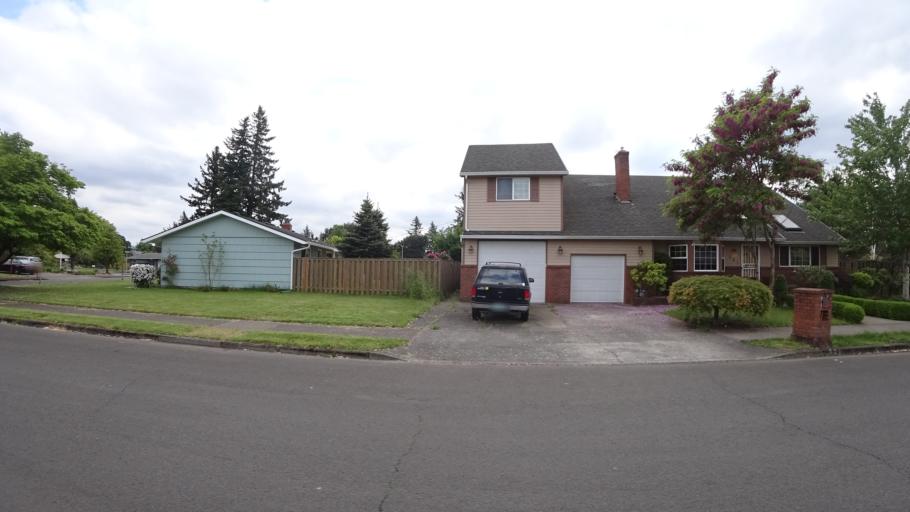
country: US
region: Oregon
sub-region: Multnomah County
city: Fairview
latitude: 45.5160
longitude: -122.4901
